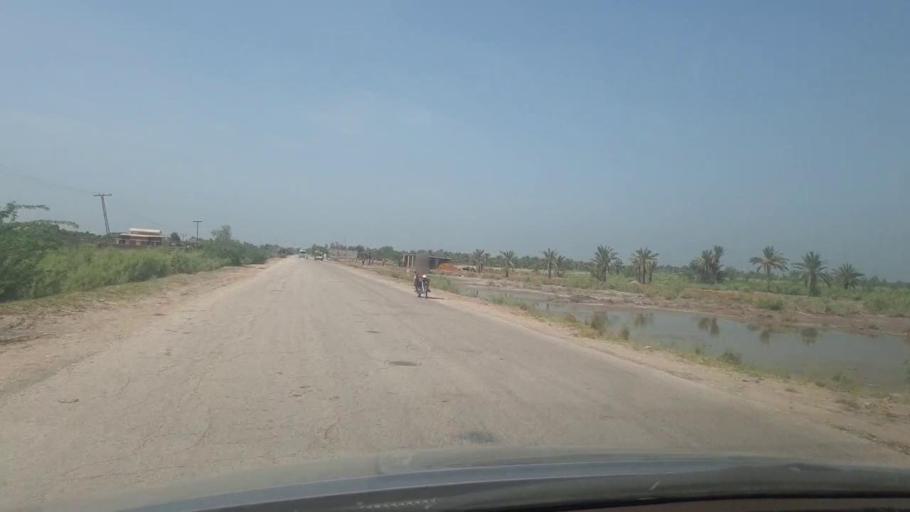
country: PK
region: Sindh
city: Ranipur
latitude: 27.2630
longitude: 68.5908
